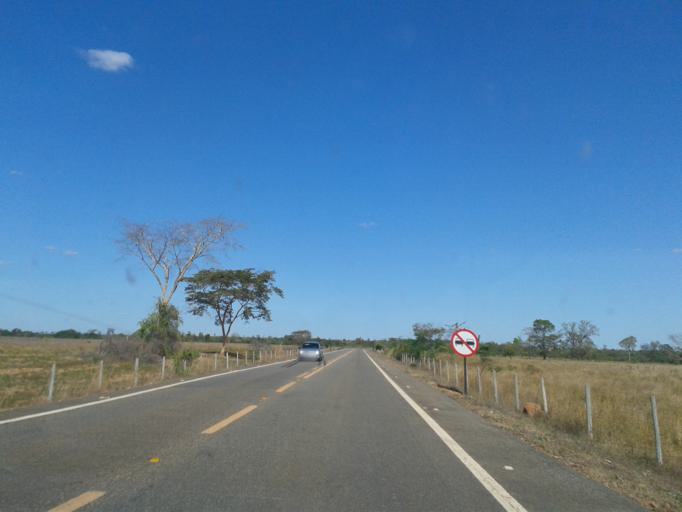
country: BR
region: Goias
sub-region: Sao Miguel Do Araguaia
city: Sao Miguel do Araguaia
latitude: -13.6256
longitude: -50.3135
